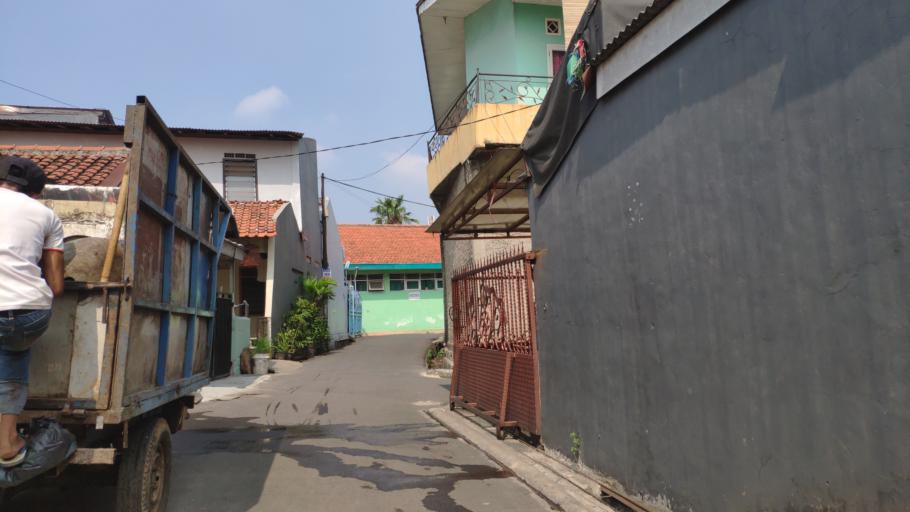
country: ID
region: Banten
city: South Tangerang
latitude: -6.2899
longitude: 106.7920
